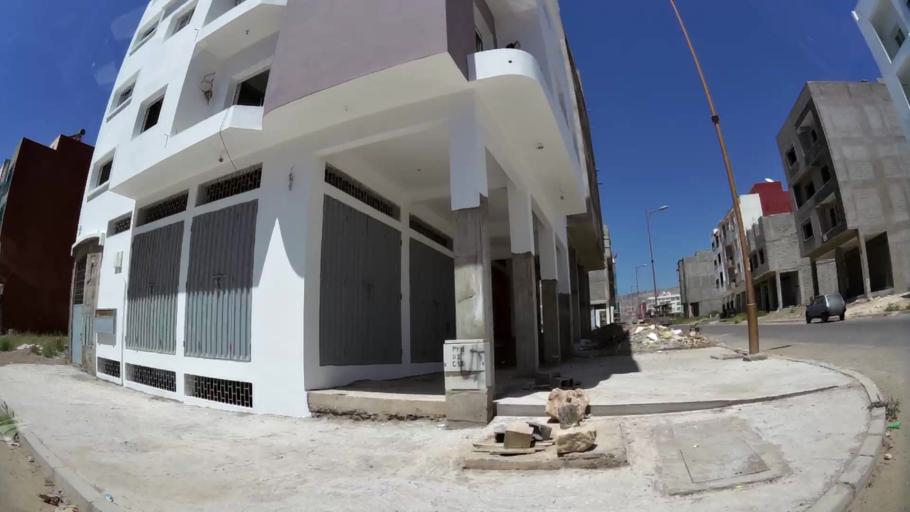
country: MA
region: Oued ed Dahab-Lagouira
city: Dakhla
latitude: 30.4376
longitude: -9.5551
